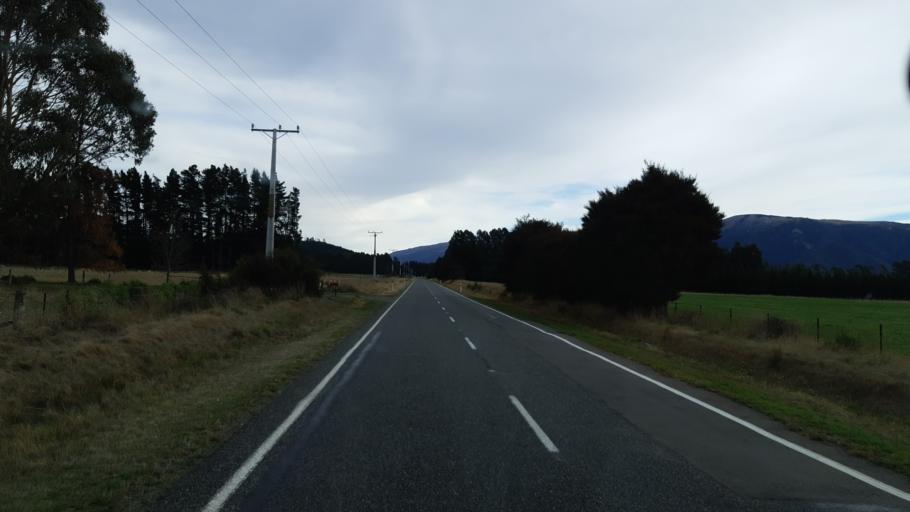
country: NZ
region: Tasman
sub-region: Tasman District
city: Brightwater
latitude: -41.6546
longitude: 173.2509
